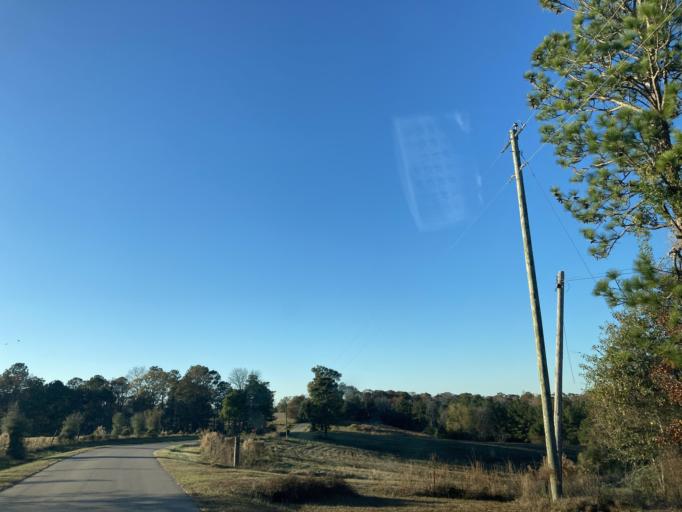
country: US
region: Mississippi
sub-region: Lamar County
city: Sumrall
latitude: 31.2674
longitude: -89.6046
